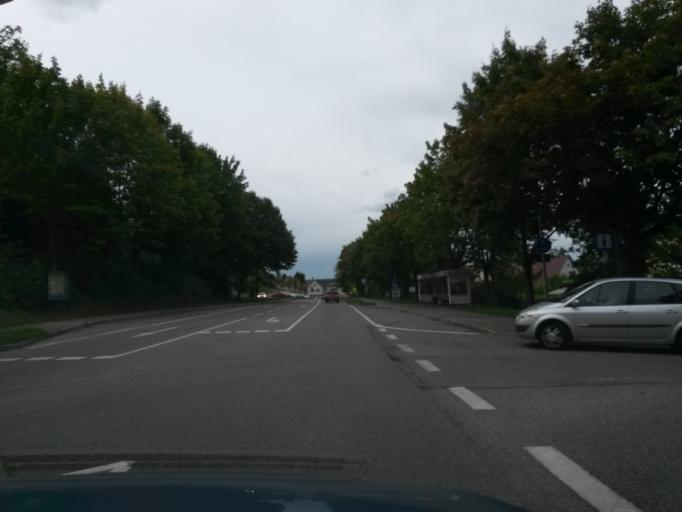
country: DE
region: Baden-Wuerttemberg
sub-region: Karlsruhe Region
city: Konigsbach-Stein
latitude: 48.9621
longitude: 8.6116
